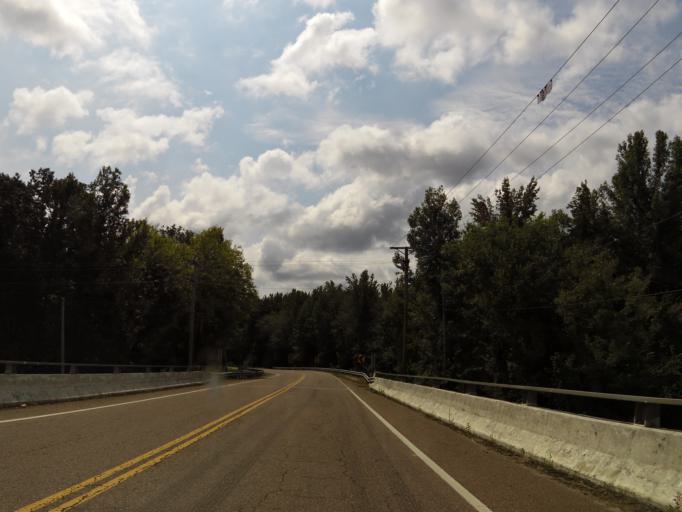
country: US
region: Tennessee
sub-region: Decatur County
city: Decaturville
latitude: 35.6171
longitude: -88.0434
